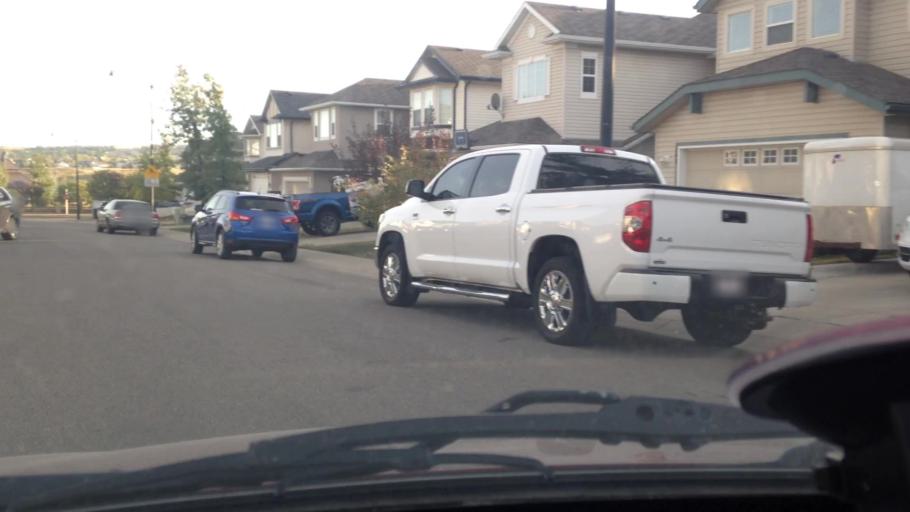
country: CA
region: Alberta
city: Calgary
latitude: 51.1627
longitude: -114.1167
